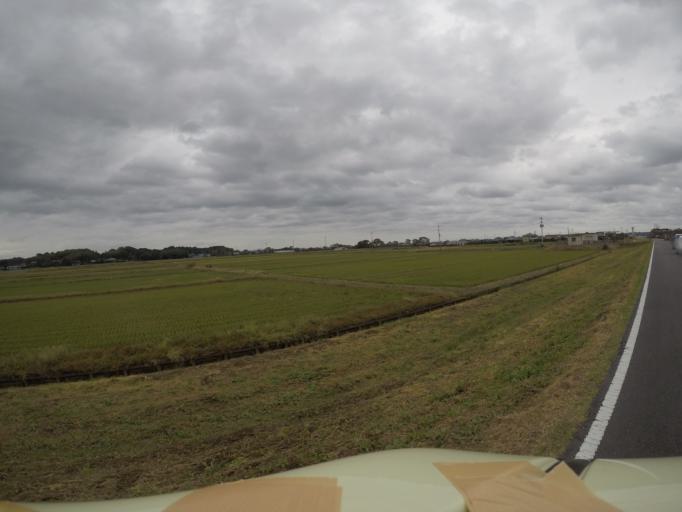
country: JP
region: Ibaraki
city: Inashiki
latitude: 36.0805
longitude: 140.3886
